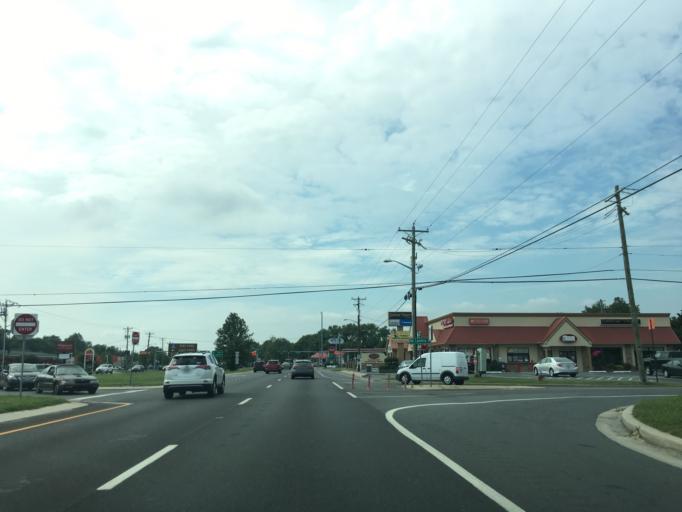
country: US
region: Delaware
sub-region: Sussex County
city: Millsboro
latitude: 38.5837
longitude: -75.2933
